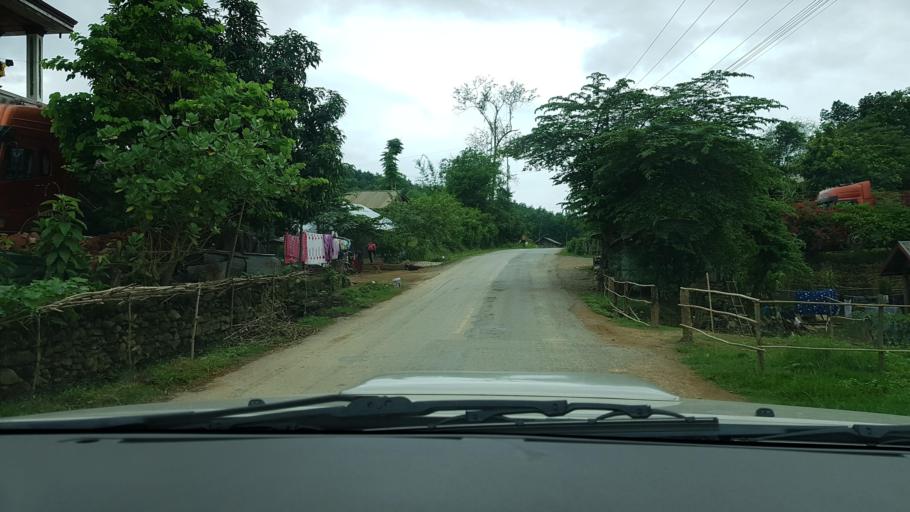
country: LA
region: Loungnamtha
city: Muang Nale
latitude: 20.2275
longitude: 101.5589
